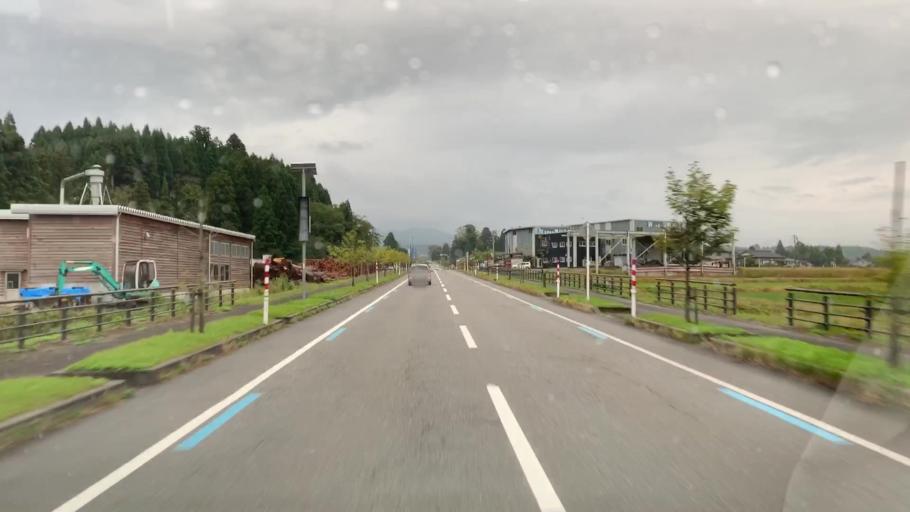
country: JP
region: Toyama
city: Kamiichi
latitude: 36.6183
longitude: 137.3276
